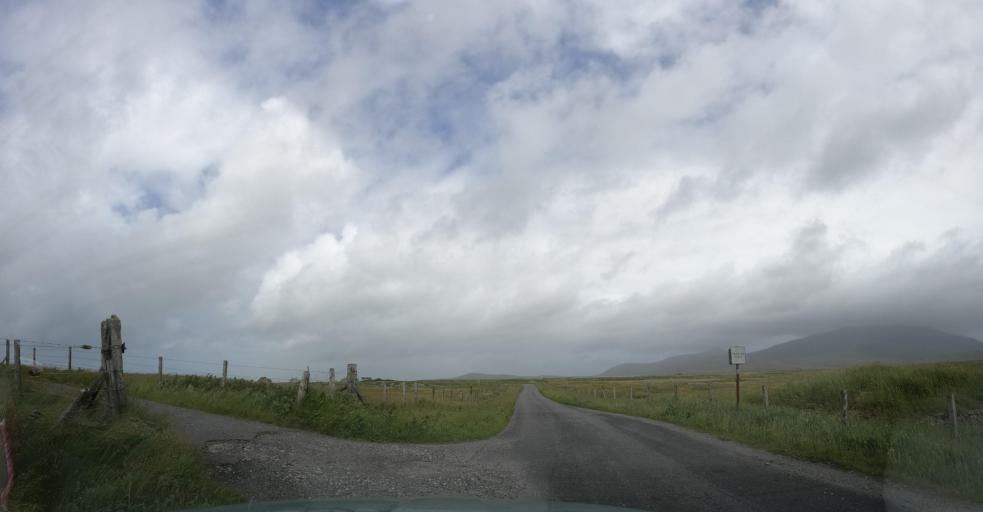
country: GB
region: Scotland
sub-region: Eilean Siar
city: Isle of South Uist
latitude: 57.2535
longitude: -7.4063
